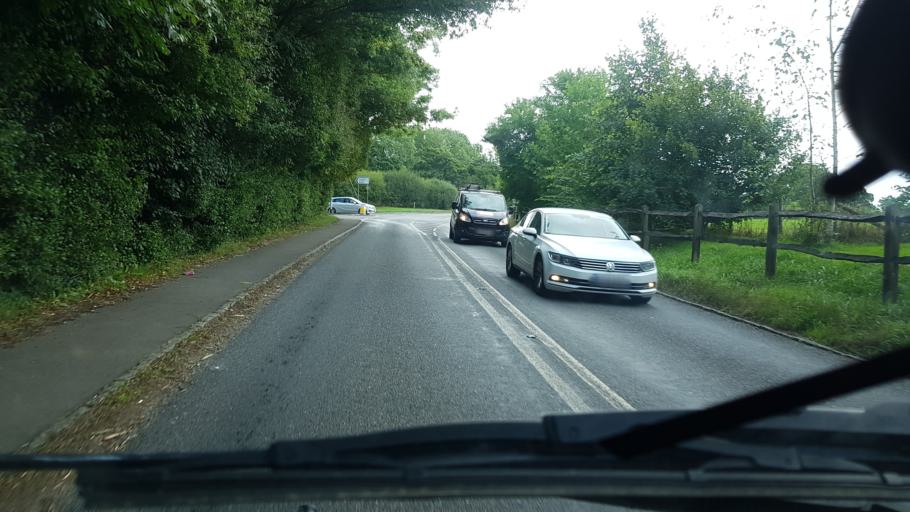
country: GB
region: England
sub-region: West Sussex
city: Rudgwick
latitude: 51.0857
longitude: -0.4543
